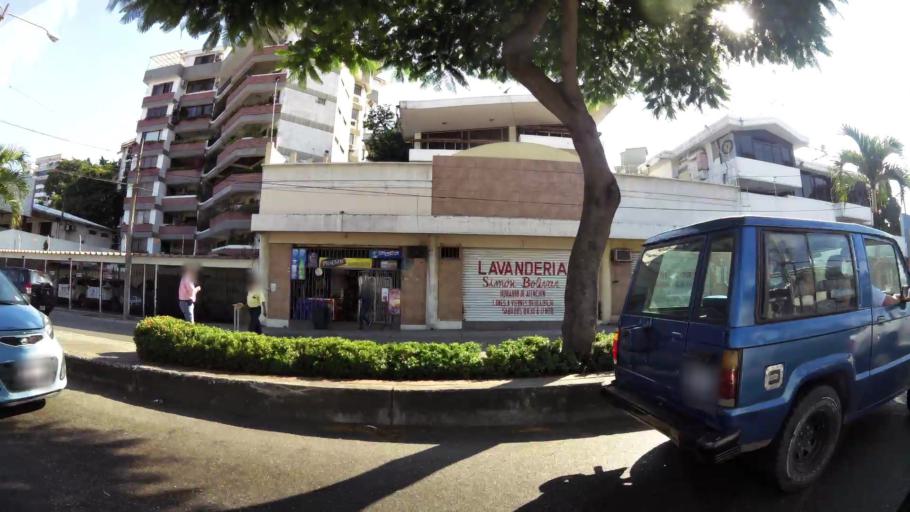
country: EC
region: Guayas
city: Guayaquil
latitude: -2.1674
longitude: -79.9036
